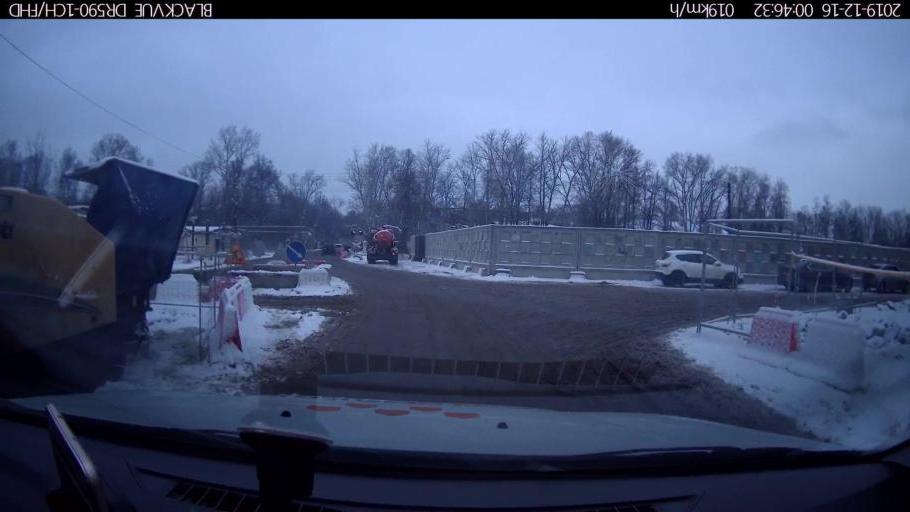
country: RU
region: Nizjnij Novgorod
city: Gorbatovka
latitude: 56.3110
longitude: 43.8583
